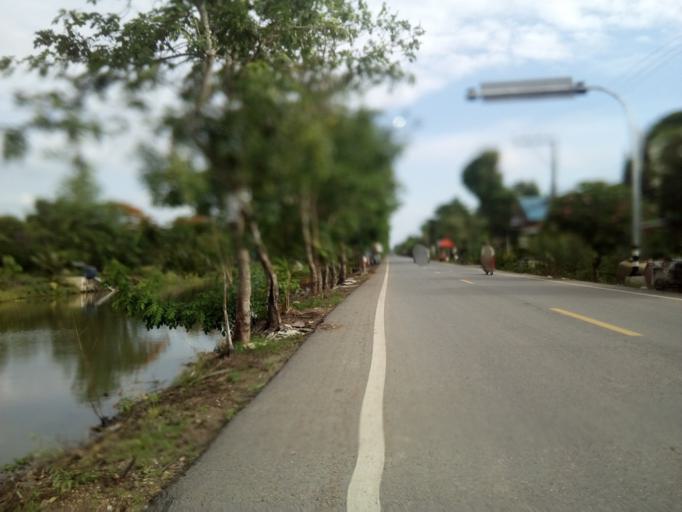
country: TH
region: Pathum Thani
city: Nong Suea
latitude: 14.1786
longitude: 100.8459
